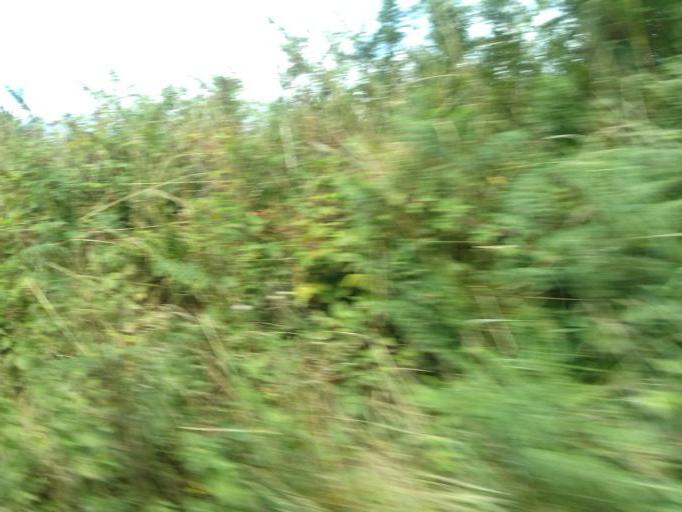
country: IE
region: Leinster
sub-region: Loch Garman
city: Ballinroad
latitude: 52.4875
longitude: -6.4469
